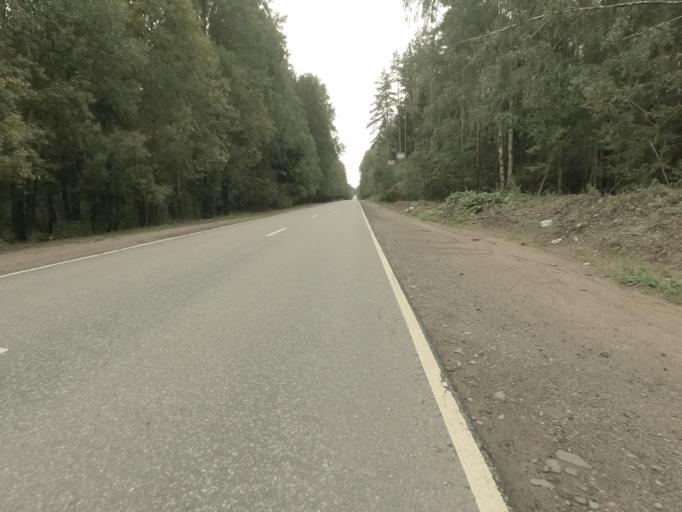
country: RU
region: Leningrad
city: Koltushi
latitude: 59.8972
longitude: 30.7567
